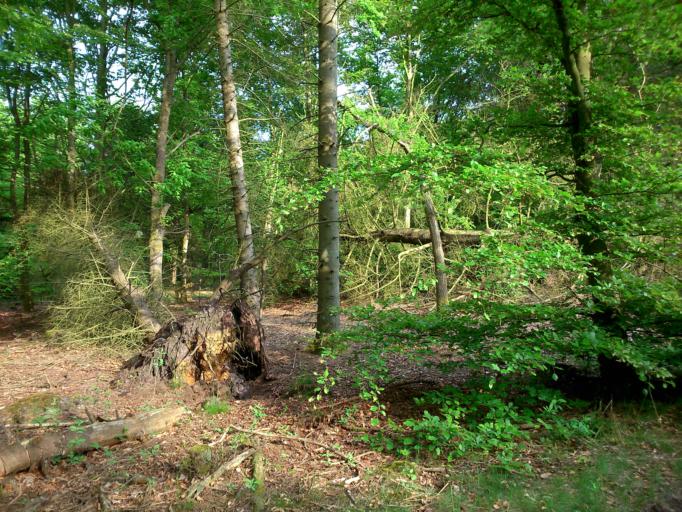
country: DK
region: Central Jutland
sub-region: Ringkobing-Skjern Kommune
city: Skjern
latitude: 55.9973
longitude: 8.4615
